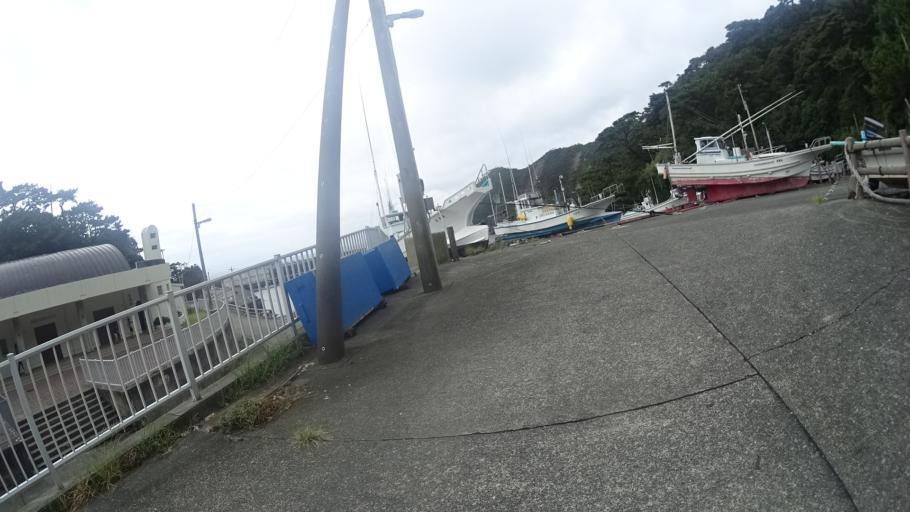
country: JP
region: Shizuoka
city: Shimoda
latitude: 34.3215
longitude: 139.2188
